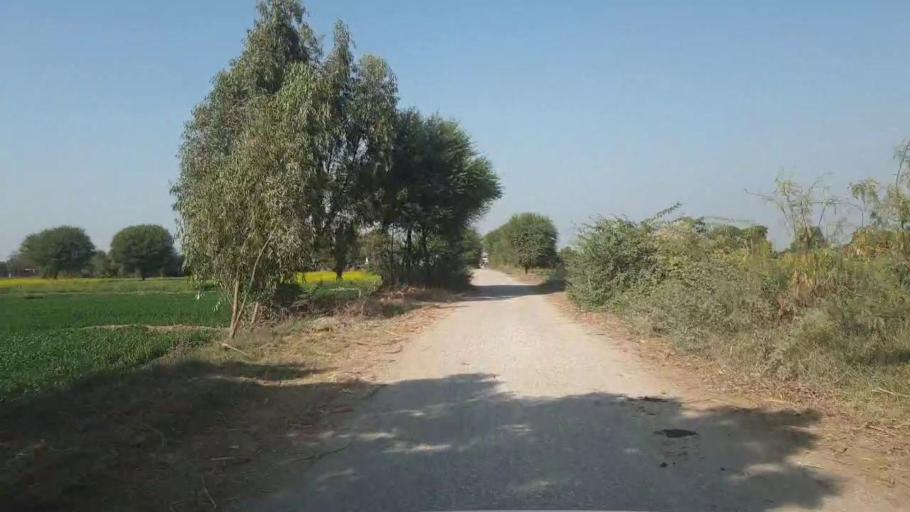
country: PK
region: Sindh
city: Chambar
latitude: 25.3066
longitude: 68.8457
